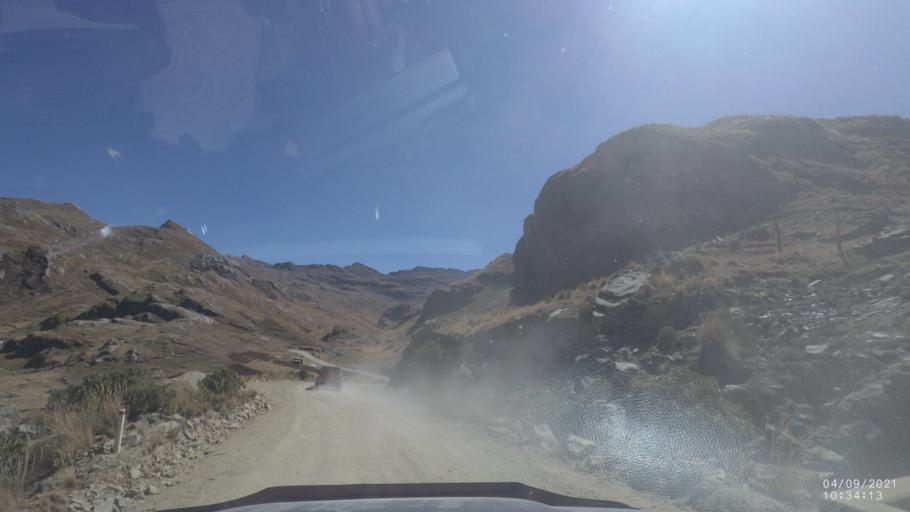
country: BO
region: Cochabamba
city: Sipe Sipe
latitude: -17.2926
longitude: -66.4450
